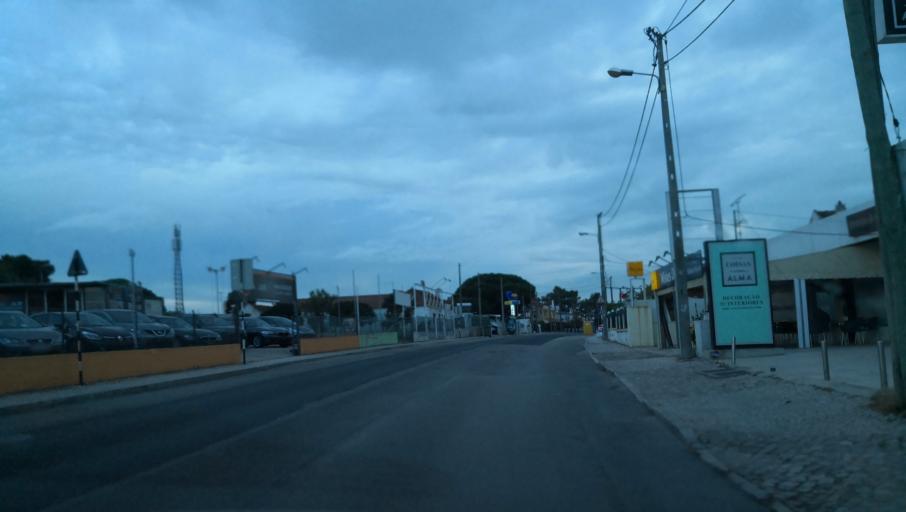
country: PT
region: Setubal
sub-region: Almada
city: Charneca
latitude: 38.6046
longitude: -9.1862
